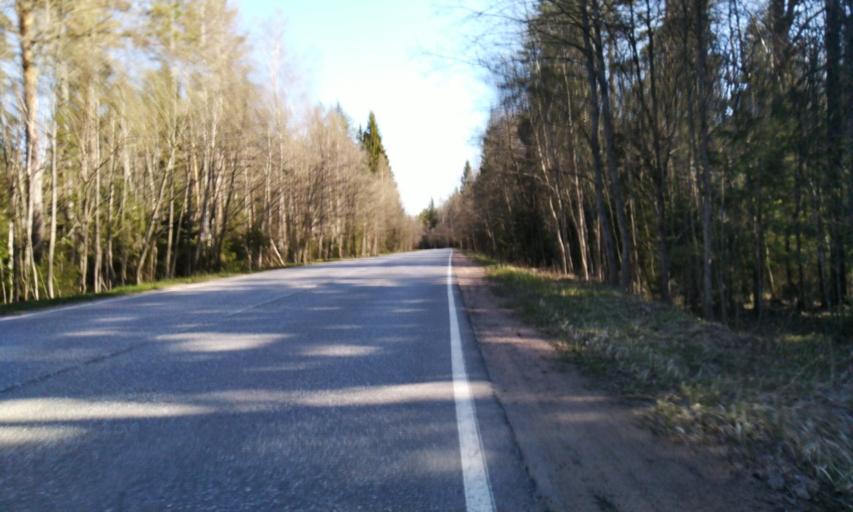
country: RU
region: Leningrad
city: Garbolovo
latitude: 60.3453
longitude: 30.4390
